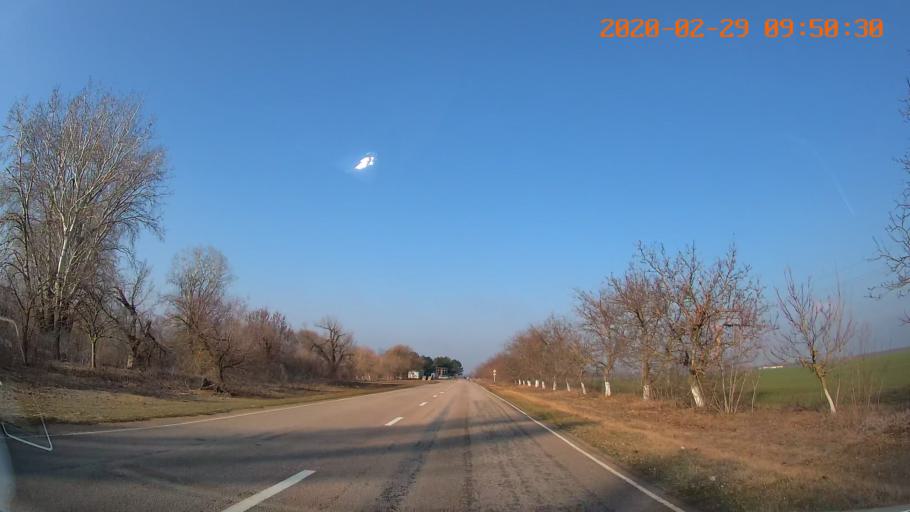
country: MD
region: Telenesti
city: Slobozia
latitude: 46.7024
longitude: 29.7545
